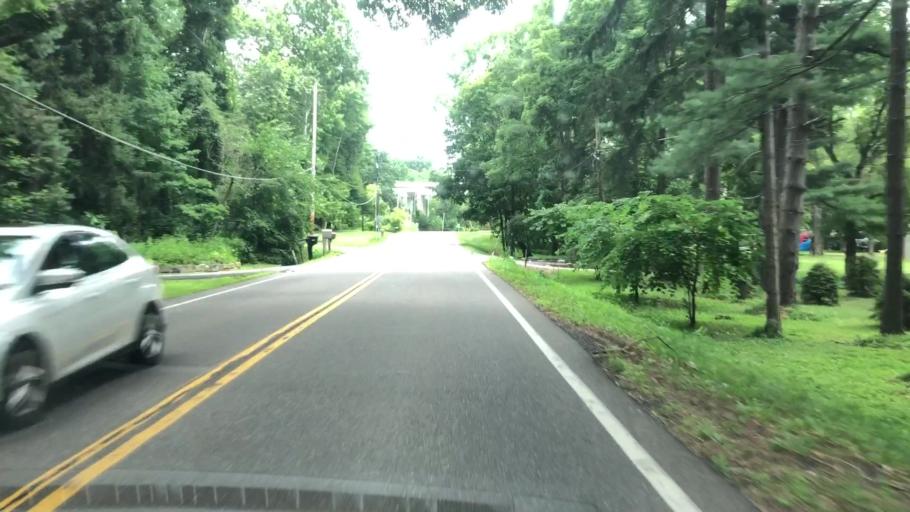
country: US
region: Ohio
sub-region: Summit County
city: Montrose-Ghent
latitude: 41.1572
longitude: -81.6300
